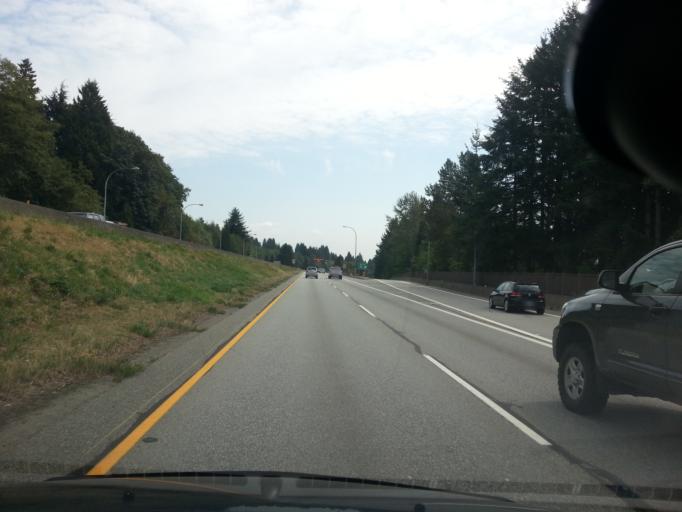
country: CA
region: British Columbia
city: West Vancouver
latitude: 49.3436
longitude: -123.1616
